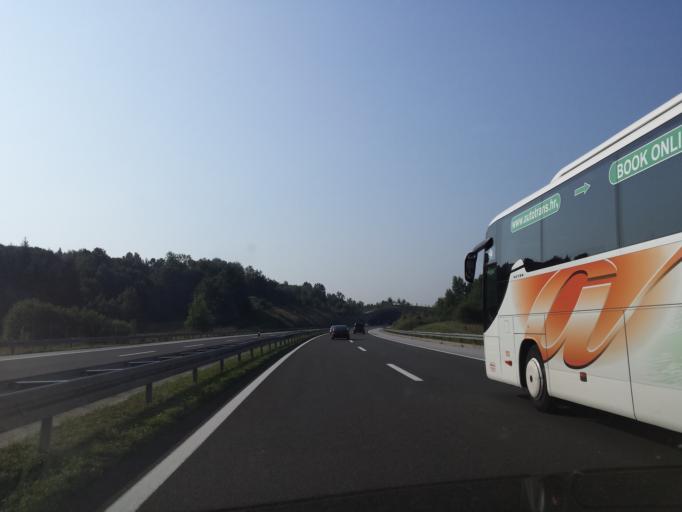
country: HR
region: Karlovacka
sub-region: Grad Ogulin
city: Ogulin
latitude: 45.3776
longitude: 15.2679
